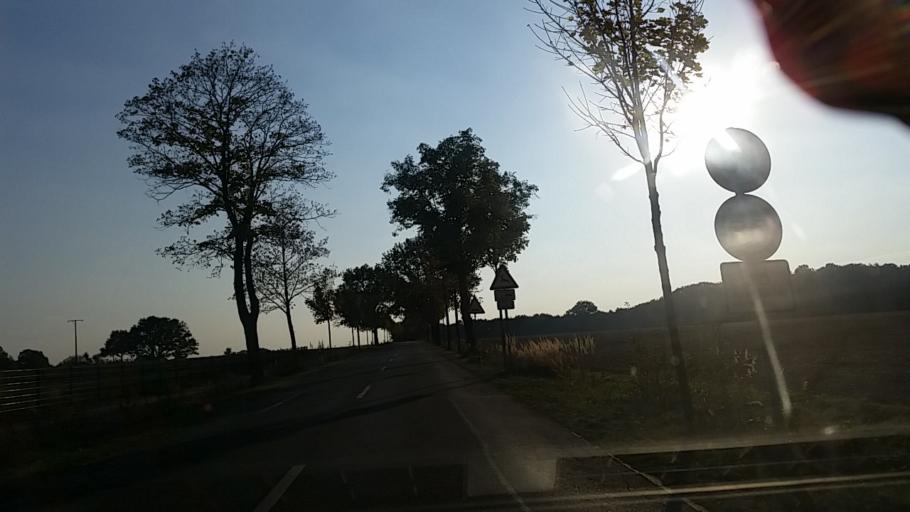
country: DE
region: Lower Saxony
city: Wolfsburg
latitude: 52.3771
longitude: 10.8000
